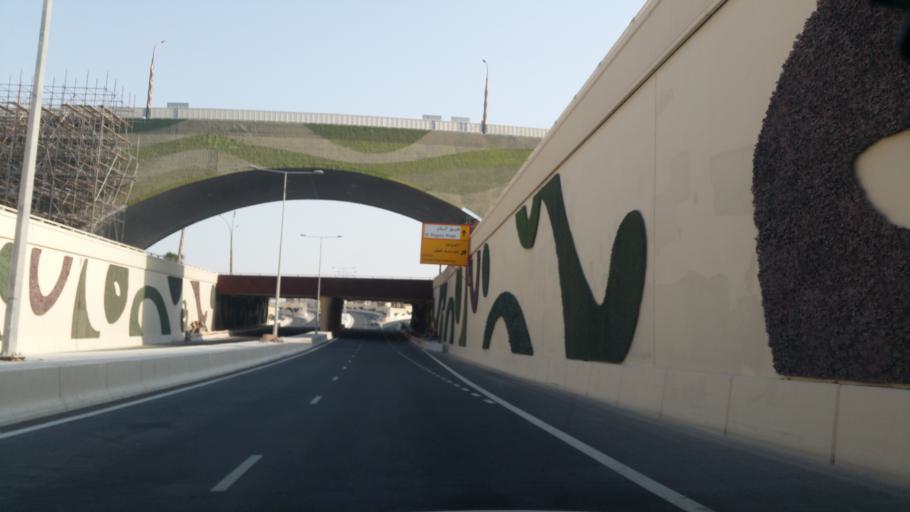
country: QA
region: Baladiyat ar Rayyan
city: Ar Rayyan
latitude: 25.3108
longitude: 51.4069
